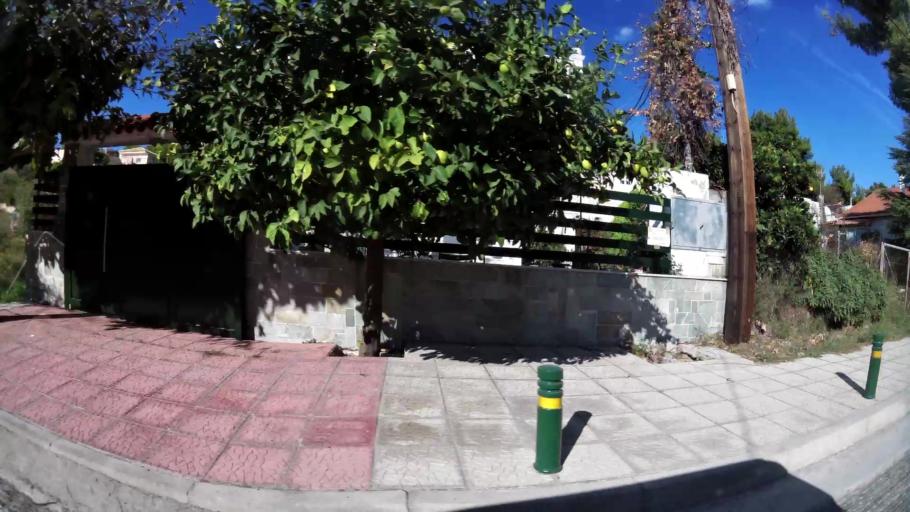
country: GR
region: Attica
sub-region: Nomarchia Anatolikis Attikis
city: Anthousa
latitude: 38.0193
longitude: 23.8748
